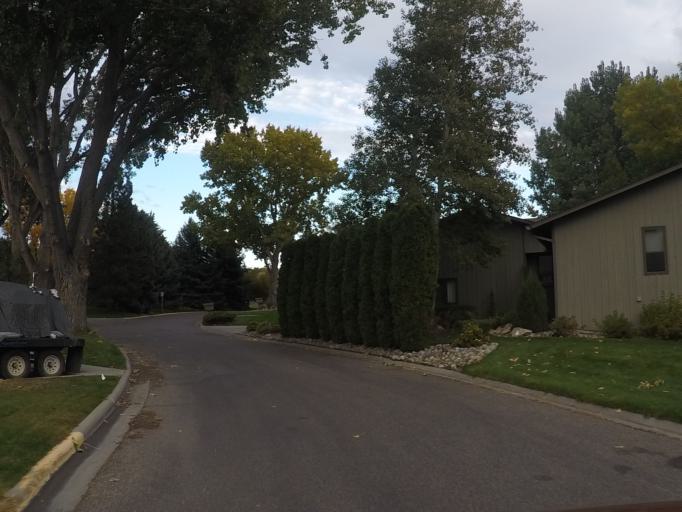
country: US
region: Montana
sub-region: Yellowstone County
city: Billings
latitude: 45.7936
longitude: -108.5533
